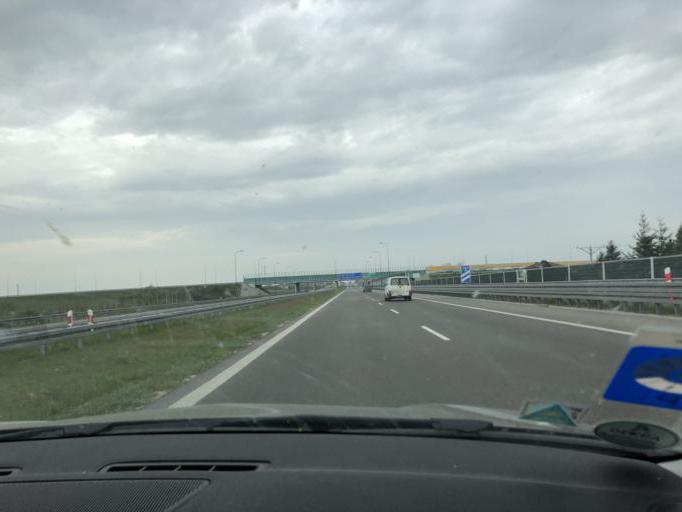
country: PL
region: Subcarpathian Voivodeship
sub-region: Powiat rzeszowski
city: Trzebownisko
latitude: 50.0932
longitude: 22.0663
